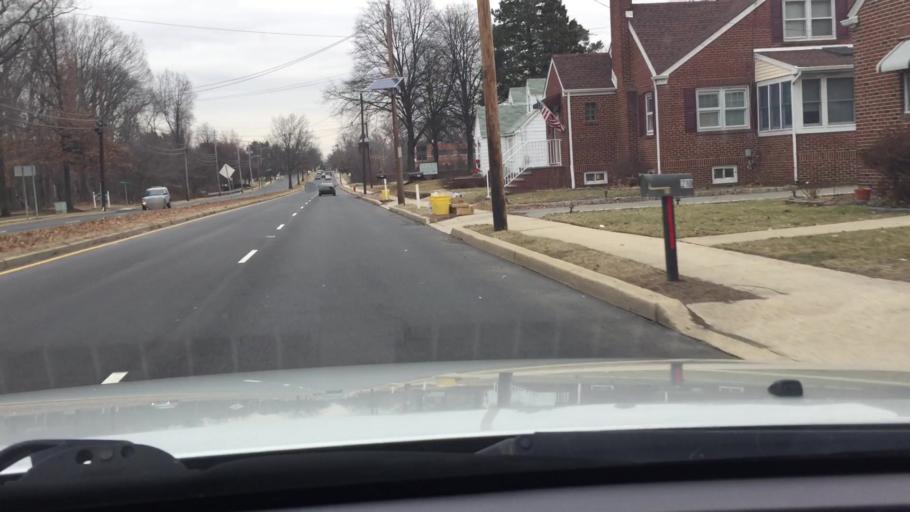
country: US
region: New Jersey
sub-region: Middlesex County
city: Old Bridge
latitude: 40.4214
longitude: -74.3894
